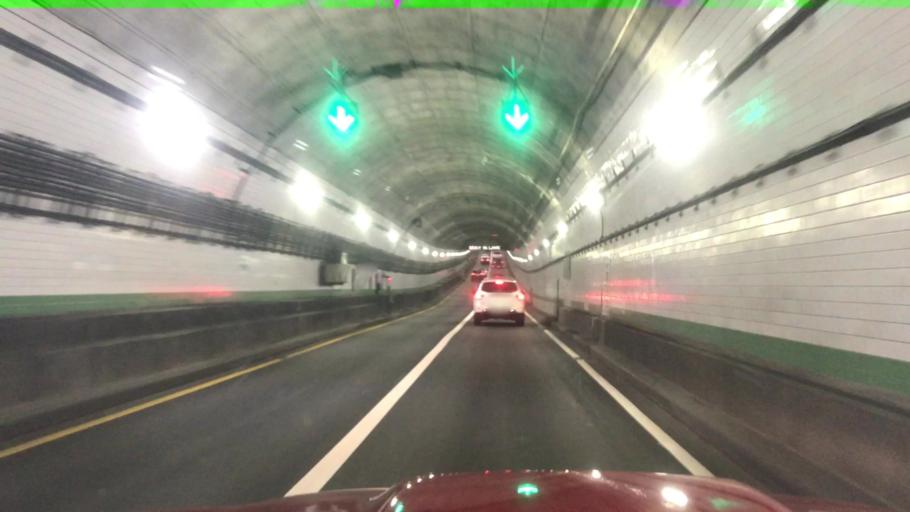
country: US
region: Virginia
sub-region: City of Portsmouth
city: Portsmouth
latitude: 36.8340
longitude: -76.2901
